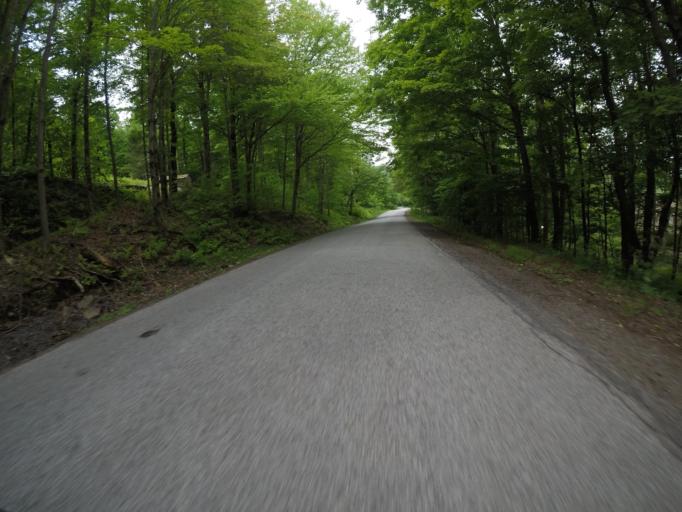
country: US
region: New York
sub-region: Delaware County
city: Stamford
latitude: 42.2570
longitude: -74.7126
